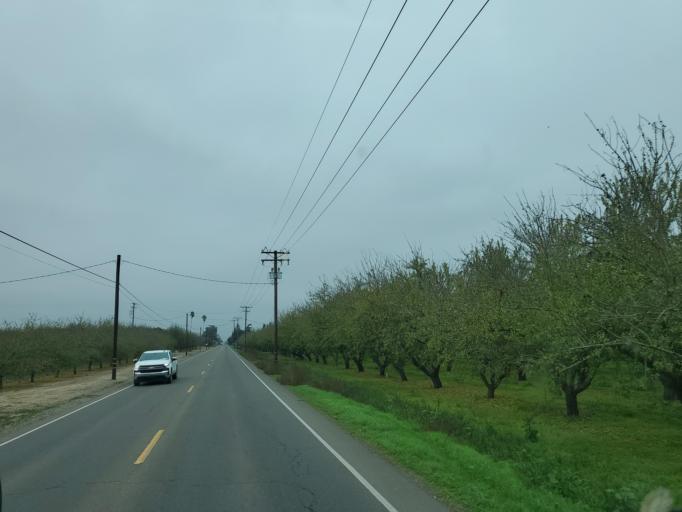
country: US
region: California
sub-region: Stanislaus County
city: Keyes
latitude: 37.5512
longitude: -120.8830
